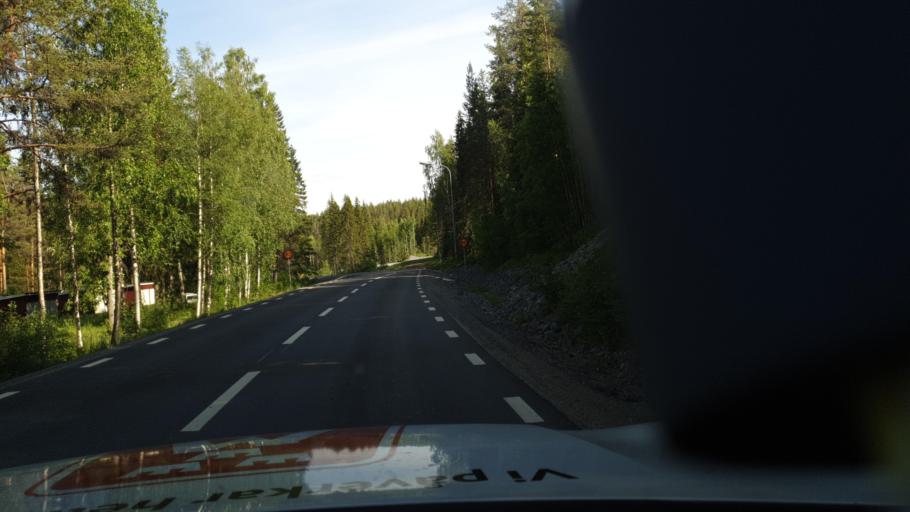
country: SE
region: Vaesterbotten
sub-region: Skelleftea Kommun
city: Boliden
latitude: 64.7901
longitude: 20.3397
